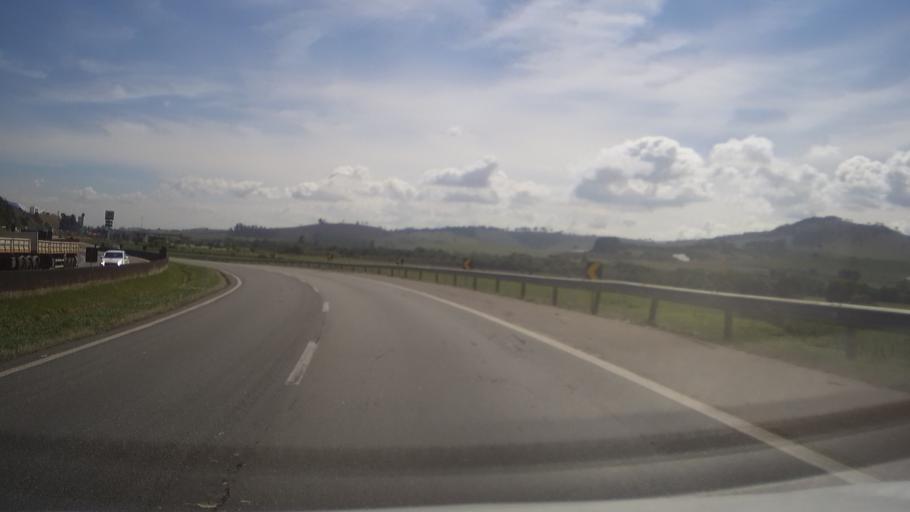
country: BR
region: Minas Gerais
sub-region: Cambui
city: Cambui
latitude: -22.5326
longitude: -46.0286
